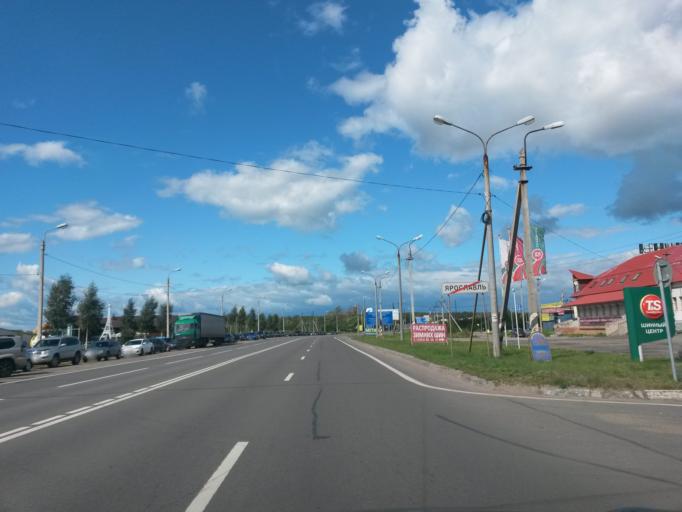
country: RU
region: Jaroslavl
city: Yaroslavl
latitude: 57.6772
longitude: 39.9029
